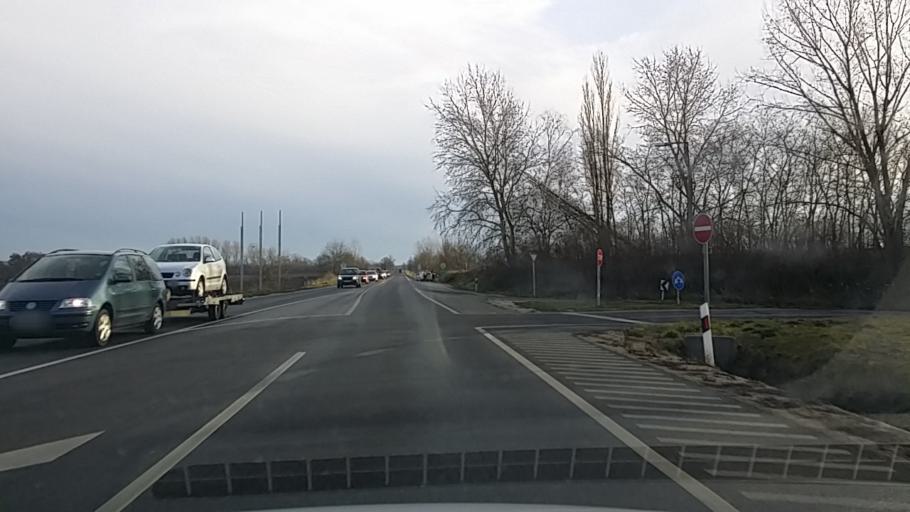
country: HU
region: Komarom-Esztergom
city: Kisber
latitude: 47.5019
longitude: 18.0458
